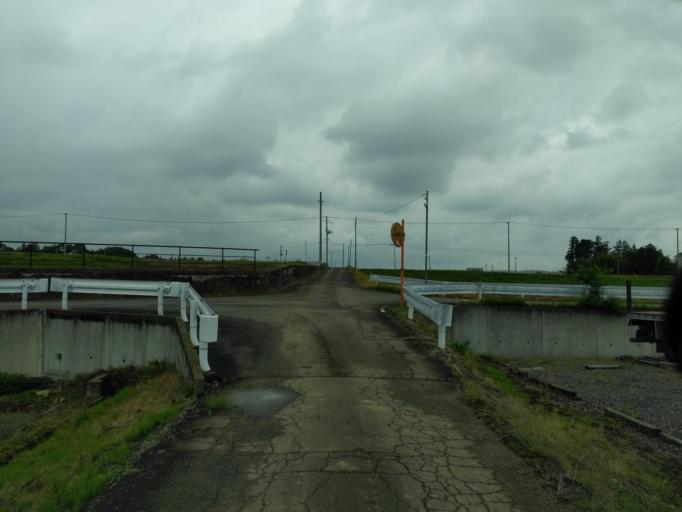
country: JP
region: Fukushima
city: Koriyama
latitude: 37.3647
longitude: 140.3337
